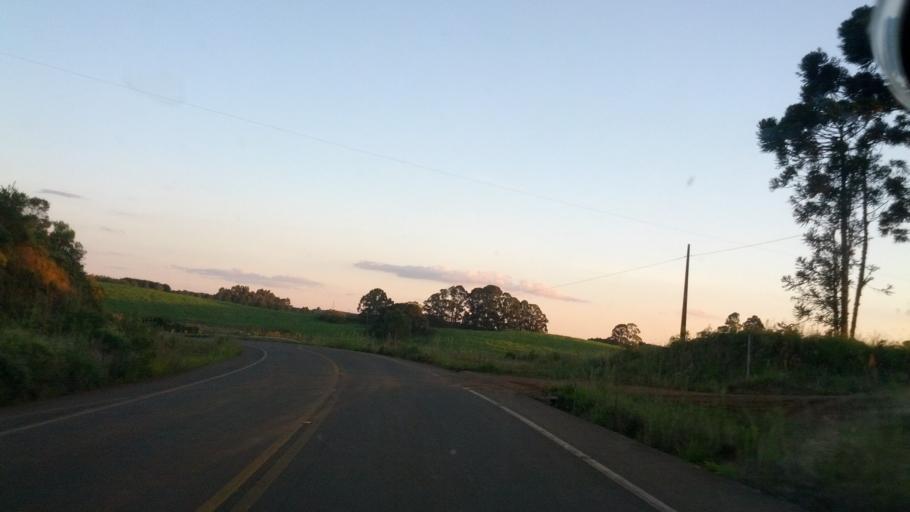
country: BR
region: Rio Grande do Sul
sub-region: Vacaria
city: Estrela
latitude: -27.8232
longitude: -50.8519
